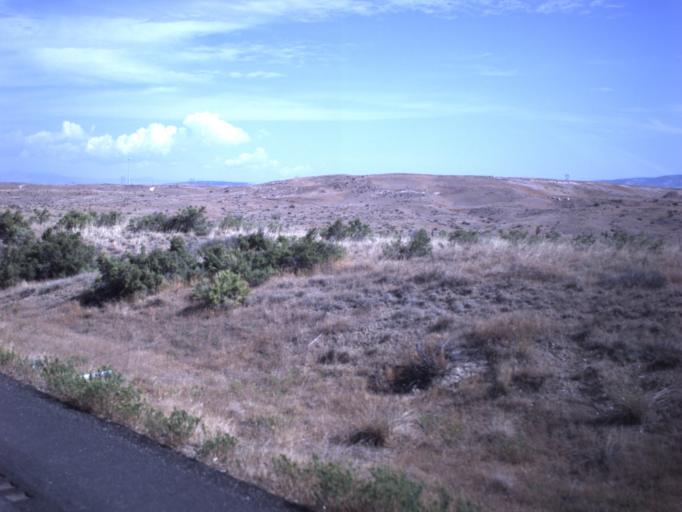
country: US
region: Utah
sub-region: Uintah County
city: Naples
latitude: 40.3614
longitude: -109.3184
